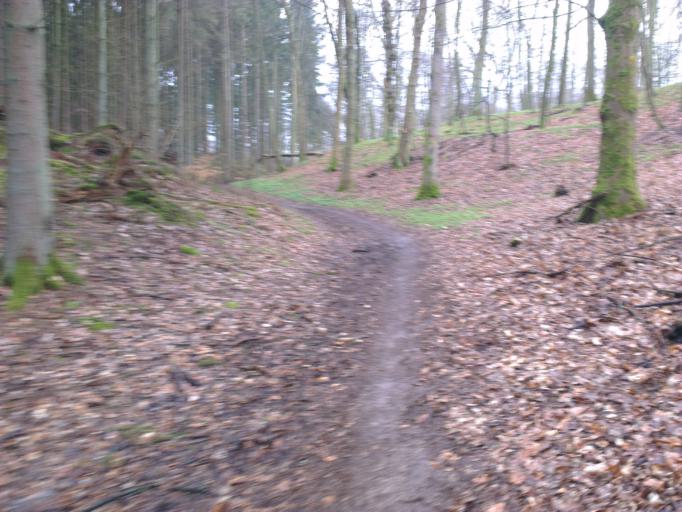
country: DK
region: Capital Region
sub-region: Frederikssund Kommune
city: Frederikssund
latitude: 55.8457
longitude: 12.0258
